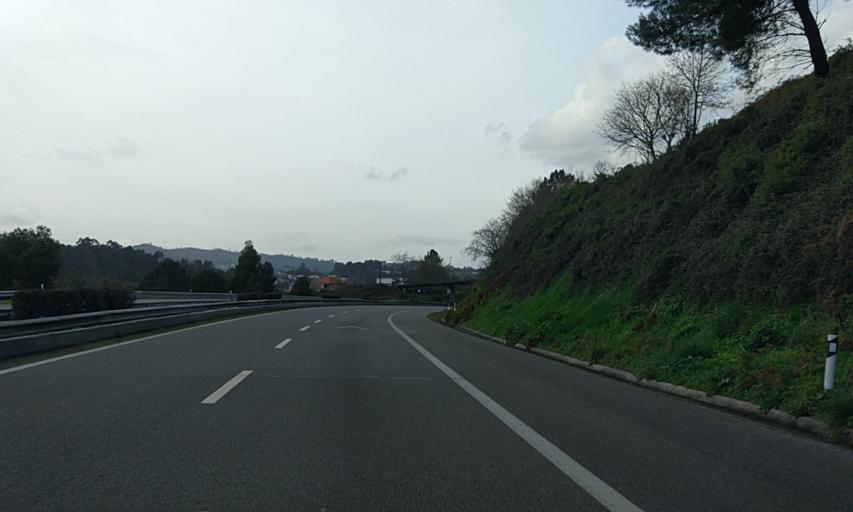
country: PT
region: Porto
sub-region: Marco de Canaveses
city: Marco de Canavezes
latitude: 41.2219
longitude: -8.1624
